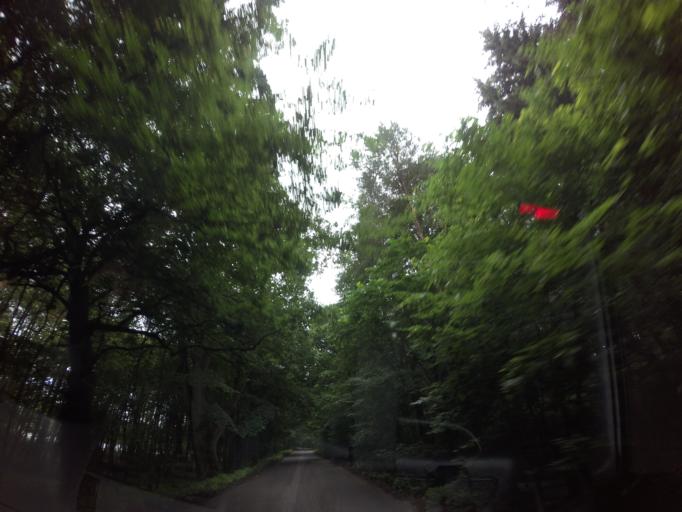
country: PL
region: West Pomeranian Voivodeship
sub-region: Powiat stargardzki
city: Insko
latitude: 53.4537
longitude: 15.6517
